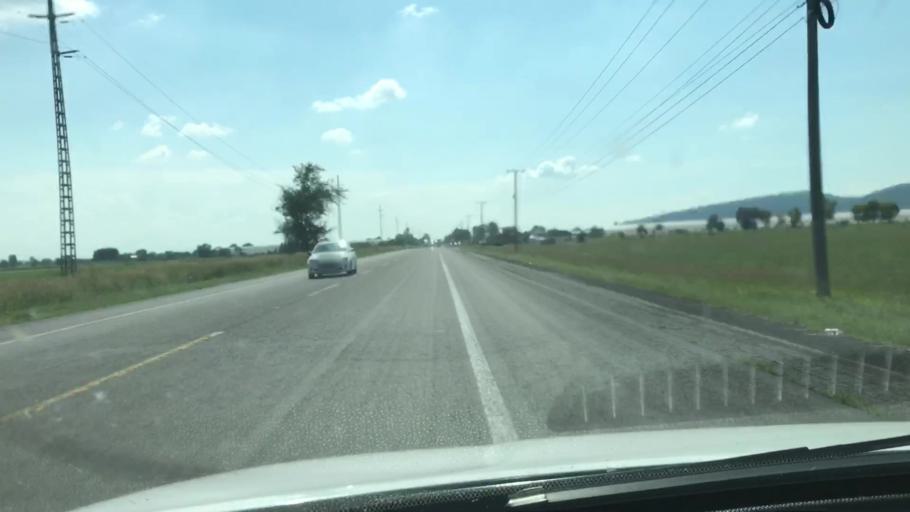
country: MX
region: Michoacan
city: Tanhuato de Guerrero
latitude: 20.2806
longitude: -102.3572
